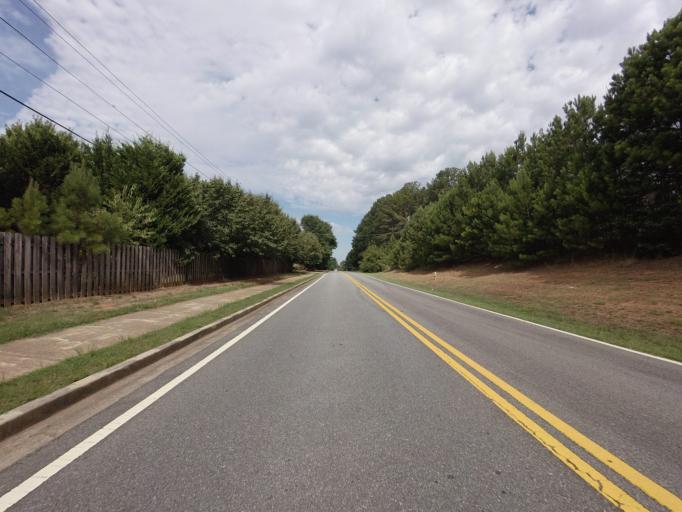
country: US
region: Georgia
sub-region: Fulton County
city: Johns Creek
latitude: 34.0425
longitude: -84.1612
